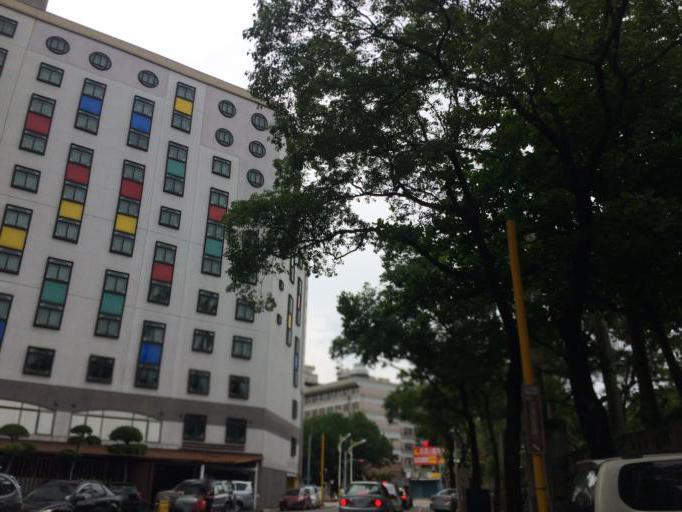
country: TW
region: Taiwan
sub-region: Hualien
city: Hualian
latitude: 23.9769
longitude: 121.6119
